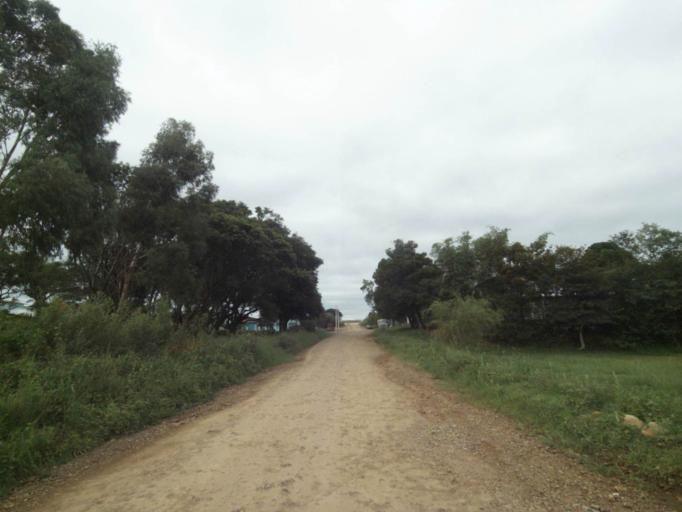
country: BR
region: Rio Grande do Sul
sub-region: Lagoa Vermelha
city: Lagoa Vermelha
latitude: -28.2182
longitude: -51.5136
